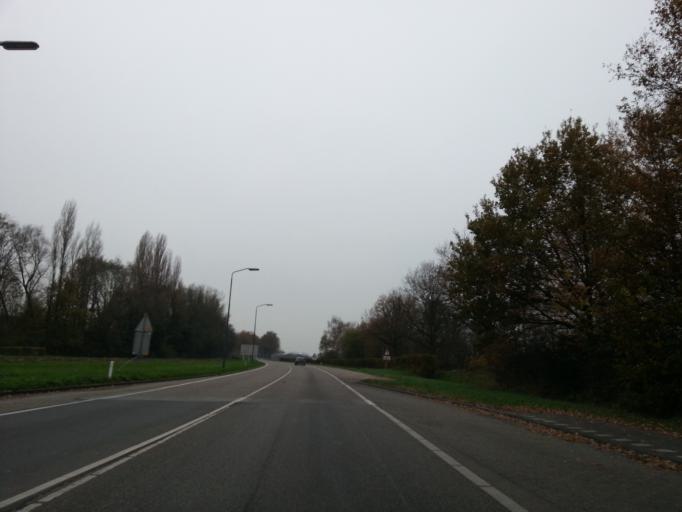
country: NL
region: North Brabant
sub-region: Gemeente Steenbergen
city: Steenbergen
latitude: 51.5702
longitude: 4.3111
